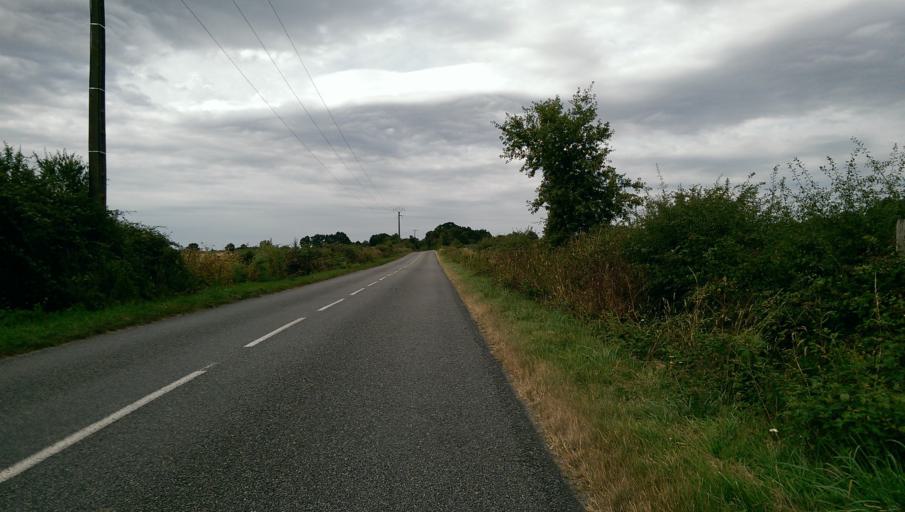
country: FR
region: Pays de la Loire
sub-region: Departement de la Loire-Atlantique
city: Vieillevigne
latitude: 46.9925
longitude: -1.4284
